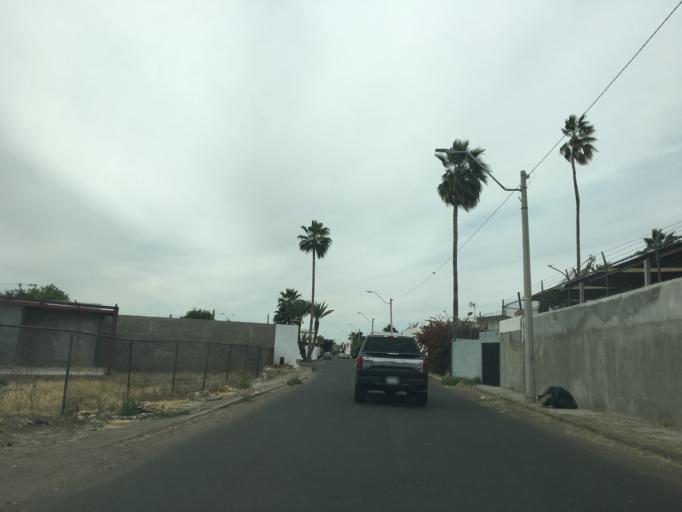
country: MX
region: Sonora
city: Hermosillo
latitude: 29.0760
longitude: -110.9687
